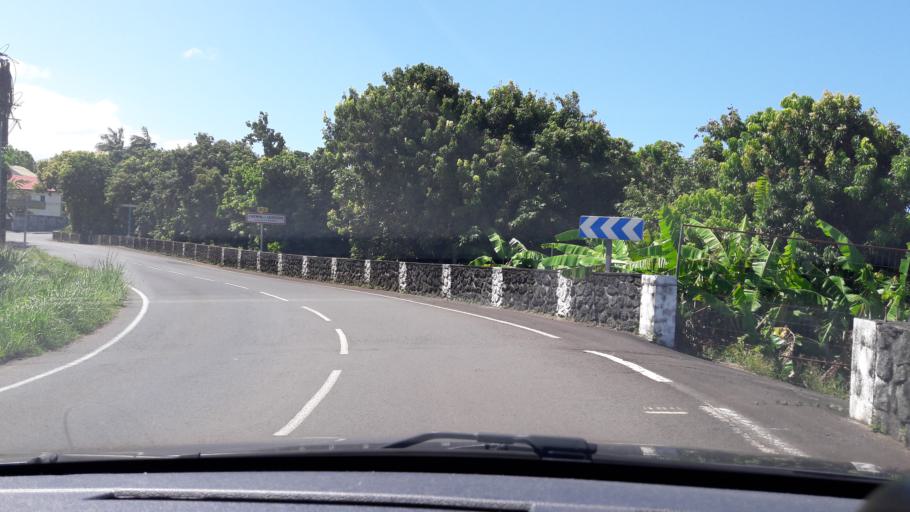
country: RE
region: Reunion
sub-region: Reunion
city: Saint-Benoit
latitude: -21.0838
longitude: 55.6952
